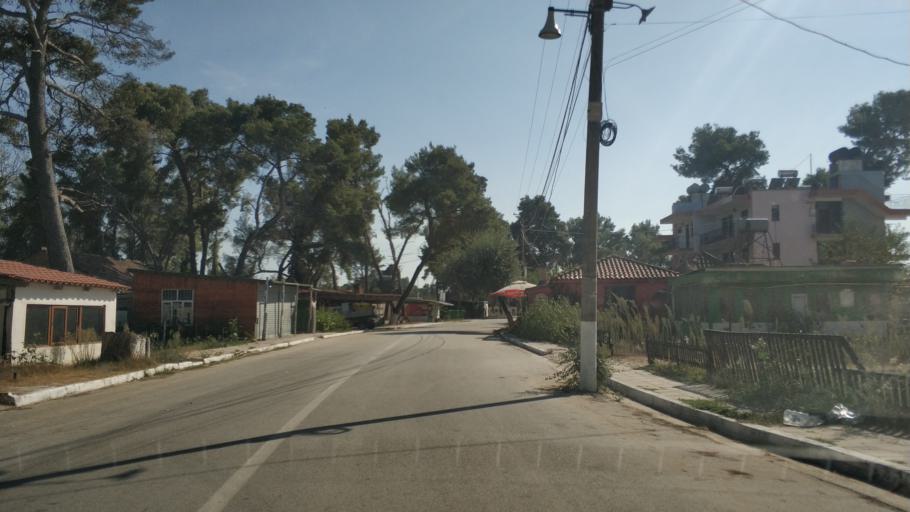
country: AL
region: Fier
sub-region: Rrethi i Lushnjes
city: Divjake
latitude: 40.9706
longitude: 19.4796
